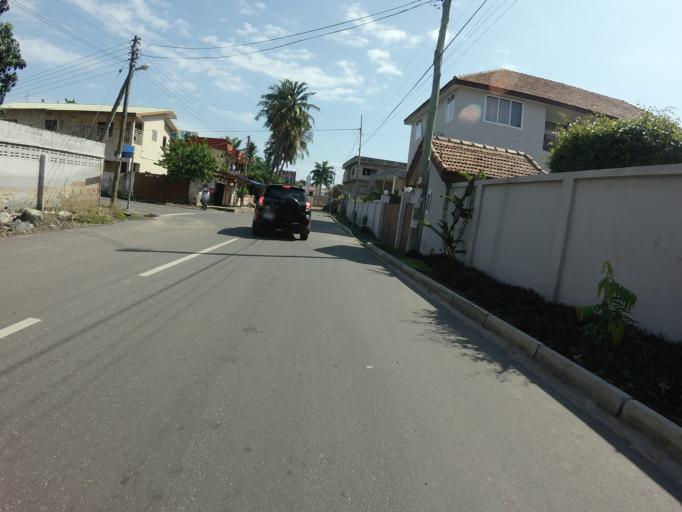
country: GH
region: Greater Accra
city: Accra
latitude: 5.5740
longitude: -0.2033
